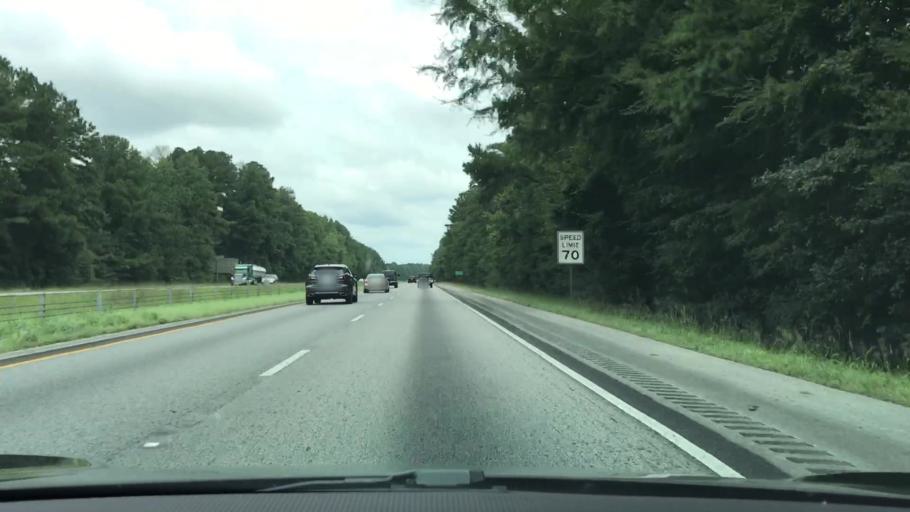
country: US
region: Alabama
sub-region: Lee County
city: Opelika
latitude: 32.7090
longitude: -85.3082
